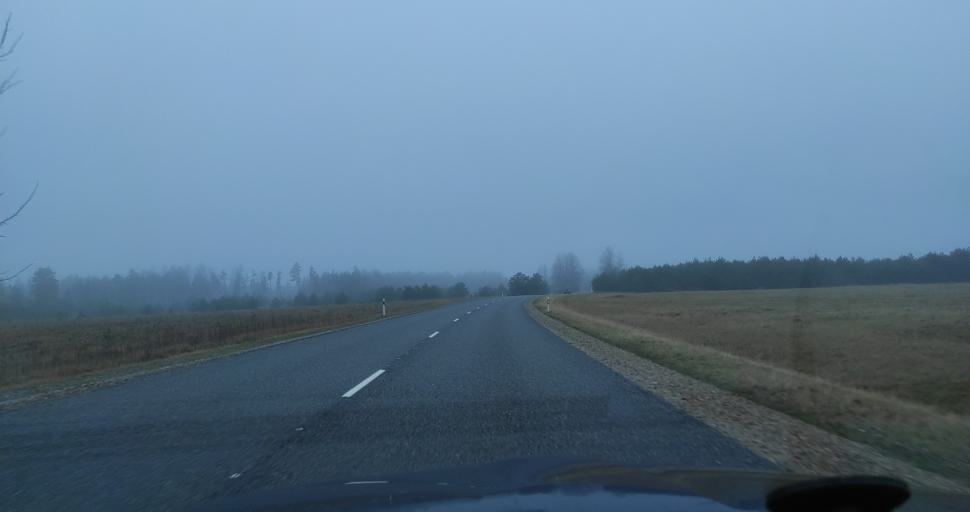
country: LV
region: Pavilostas
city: Pavilosta
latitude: 56.9526
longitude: 21.3135
